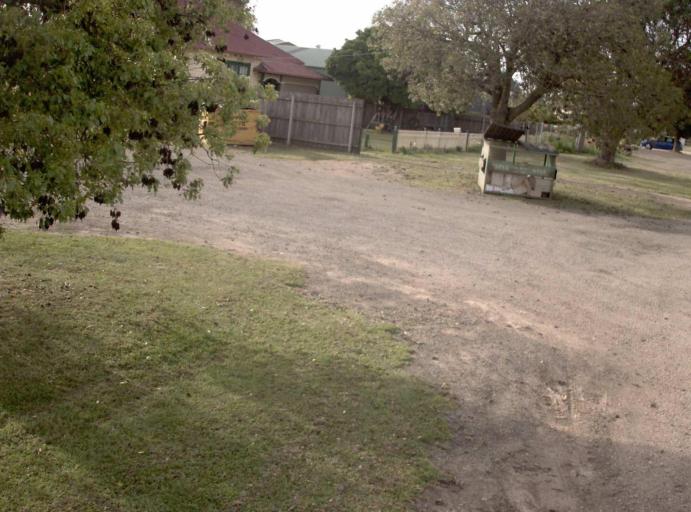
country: AU
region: Victoria
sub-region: Wellington
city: Sale
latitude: -37.9743
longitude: 146.9856
